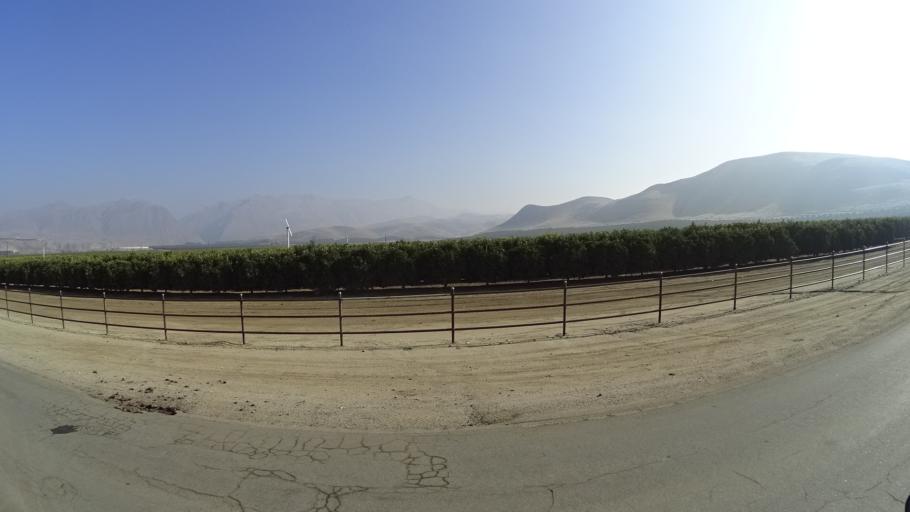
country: US
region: California
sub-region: Kern County
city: Lamont
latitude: 35.4197
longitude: -118.8326
